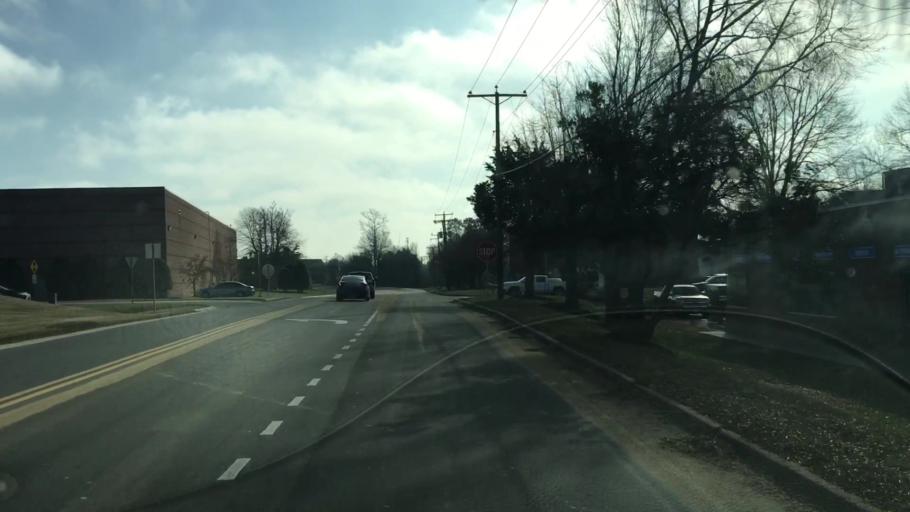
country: US
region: Virginia
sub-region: Chesterfield County
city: Bon Air
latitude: 37.5094
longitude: -77.6166
